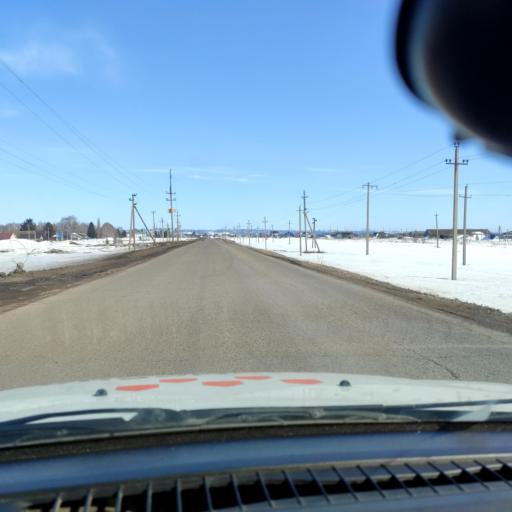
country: RU
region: Bashkortostan
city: Mikhaylovka
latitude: 54.8898
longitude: 55.9125
